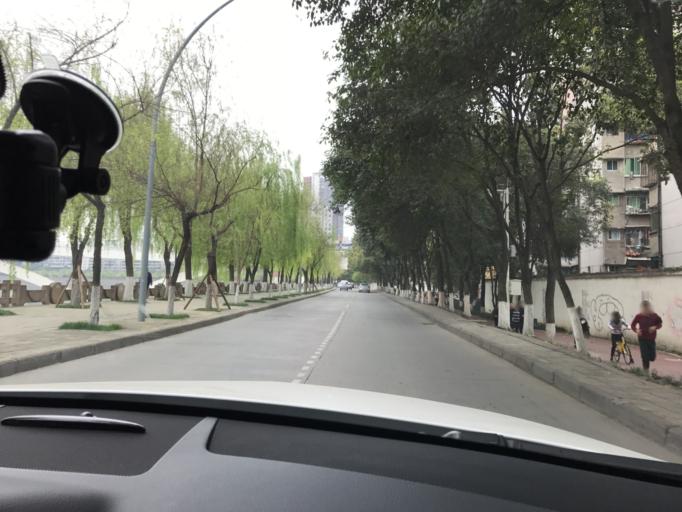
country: CN
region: Sichuan
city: Mianyang
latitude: 31.4574
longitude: 104.7463
